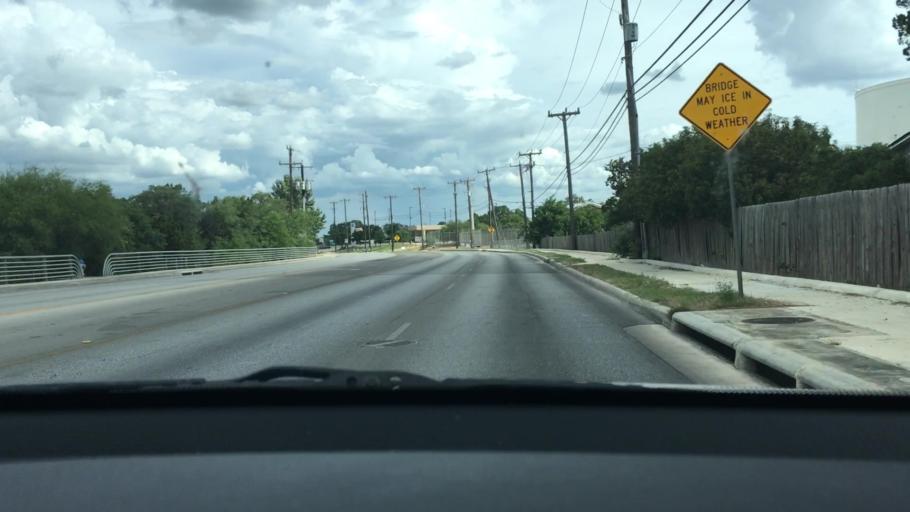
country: US
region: Texas
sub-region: Bexar County
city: Timberwood Park
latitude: 29.6503
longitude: -98.4261
